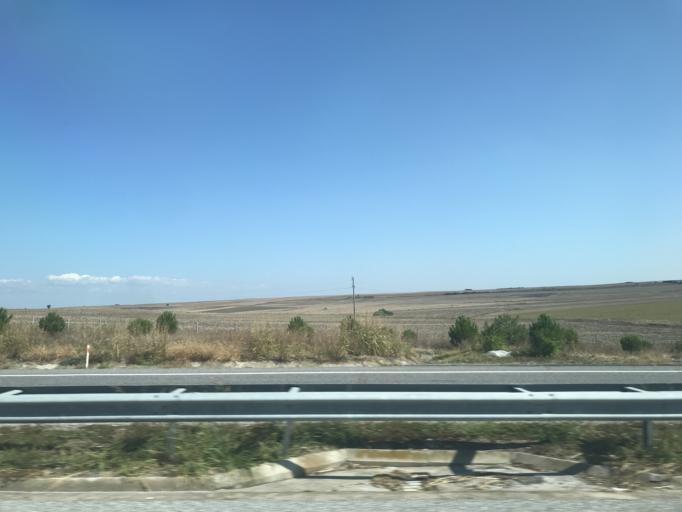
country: TR
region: Kirklareli
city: Luleburgaz
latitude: 41.4241
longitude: 27.3843
